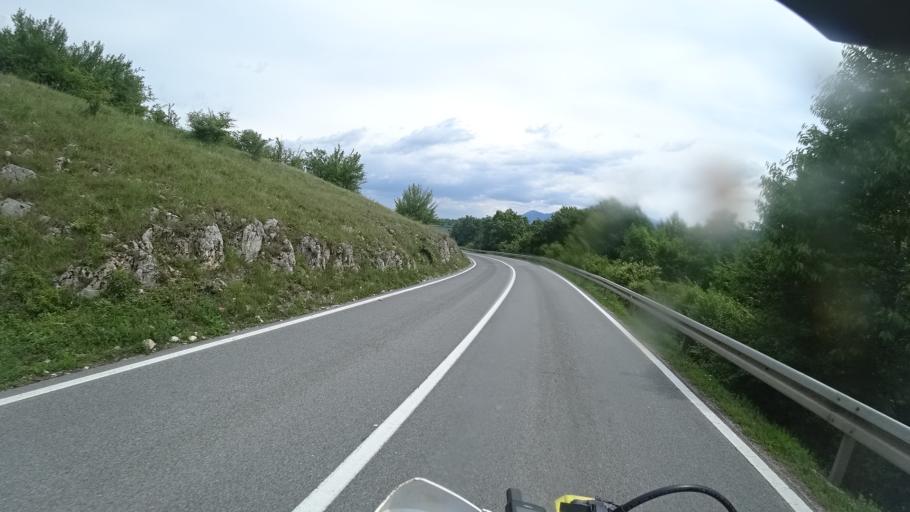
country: BA
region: Federation of Bosnia and Herzegovina
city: Izacic
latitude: 44.9213
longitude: 15.7048
